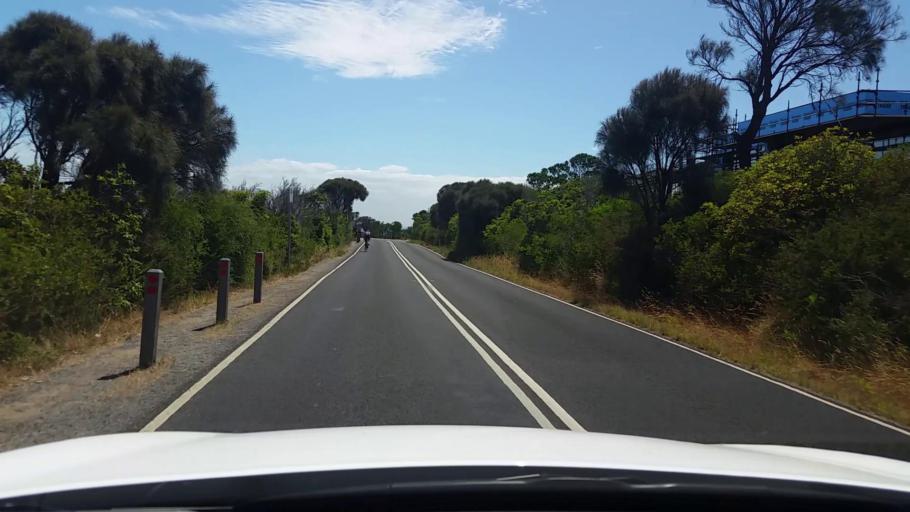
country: AU
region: Victoria
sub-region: Mornington Peninsula
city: Mount Martha
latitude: -38.2728
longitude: 145.0016
